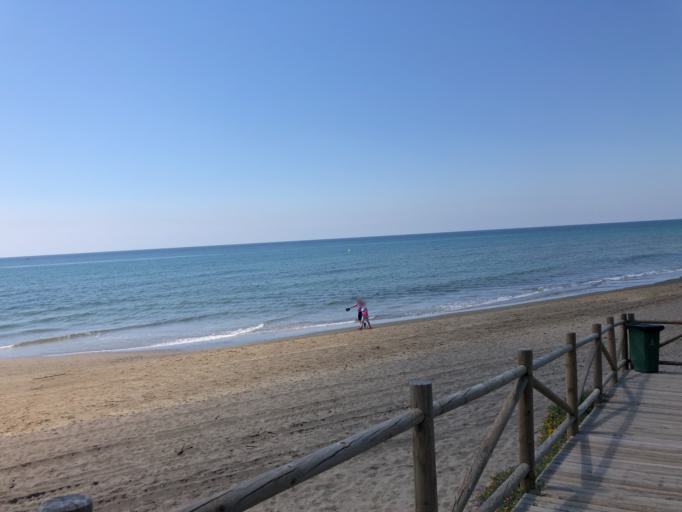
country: ES
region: Andalusia
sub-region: Provincia de Malaga
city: Fuengirola
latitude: 36.4853
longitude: -4.7472
